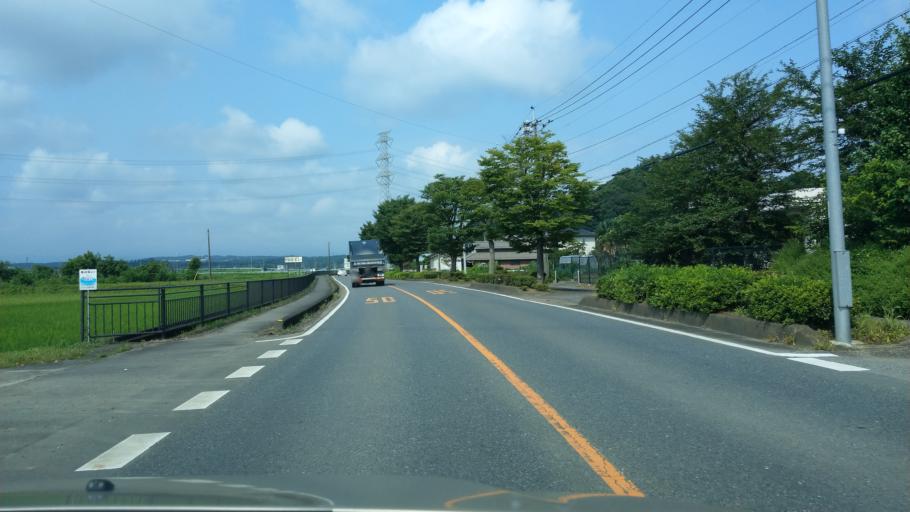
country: JP
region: Saitama
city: Sakado
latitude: 36.0170
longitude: 139.4153
